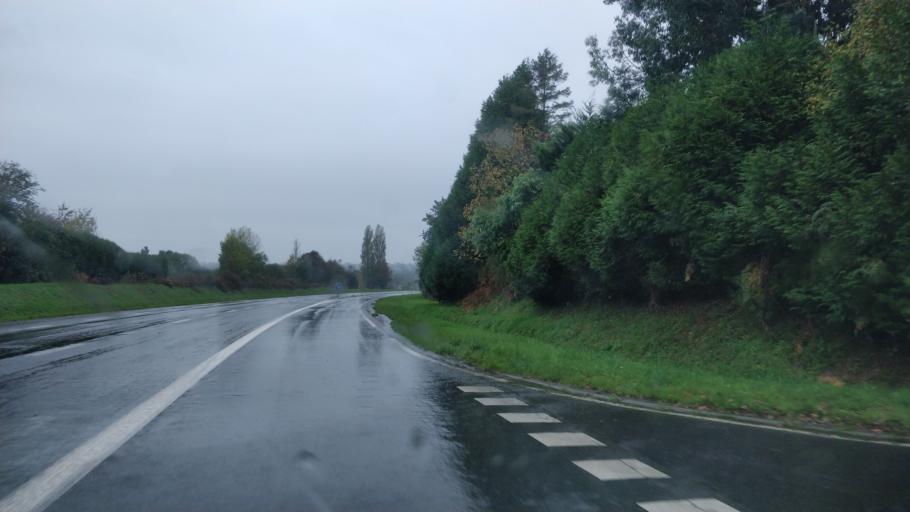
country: FR
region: Lower Normandy
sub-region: Departement de la Manche
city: Saint-Planchers
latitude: 48.8618
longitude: -1.5389
